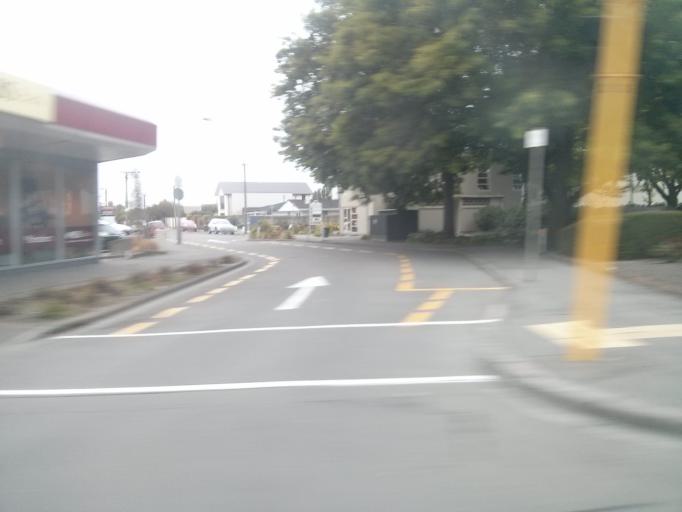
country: NZ
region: Canterbury
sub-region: Christchurch City
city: Christchurch
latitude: -43.4969
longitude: 172.6080
